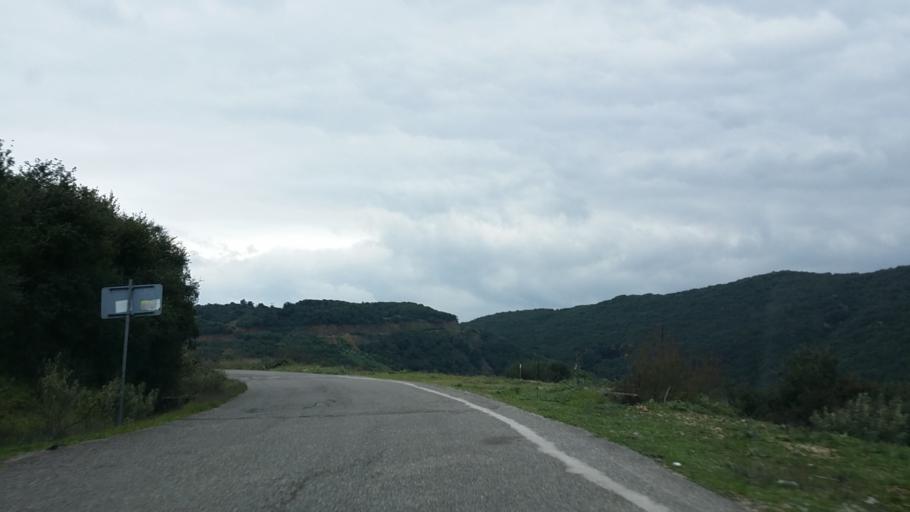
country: GR
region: West Greece
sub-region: Nomos Aitolias kai Akarnanias
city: Fitiai
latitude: 38.7175
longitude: 21.1716
